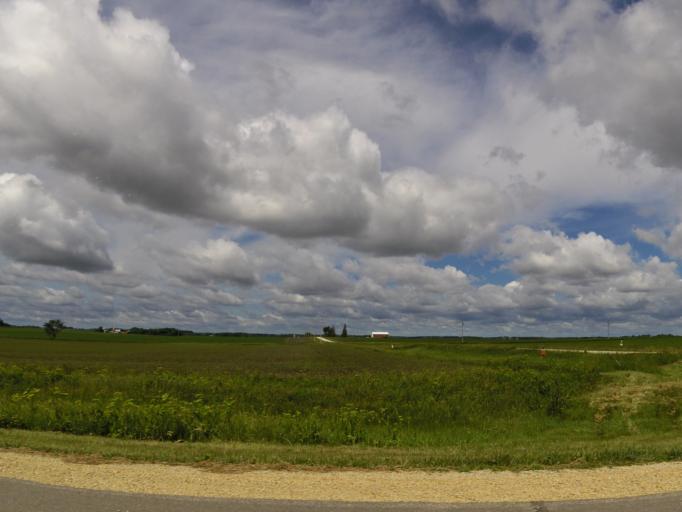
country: US
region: Minnesota
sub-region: Olmsted County
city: Stewartville
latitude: 43.7976
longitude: -92.4904
